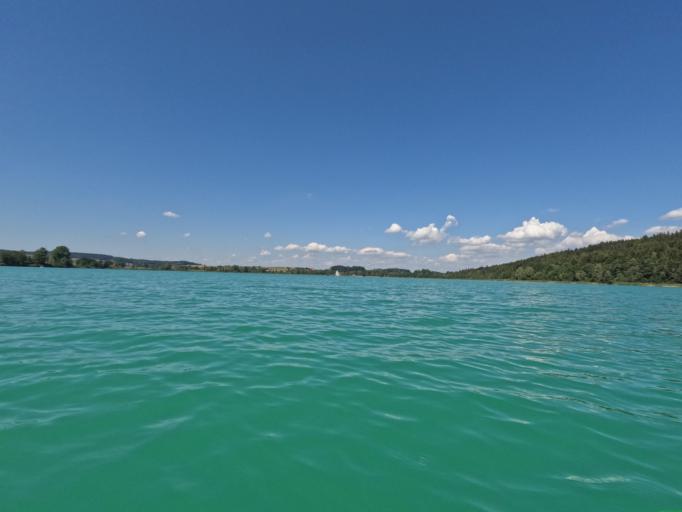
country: DE
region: Bavaria
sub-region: Upper Bavaria
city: Taching am See
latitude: 47.9770
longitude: 12.7452
